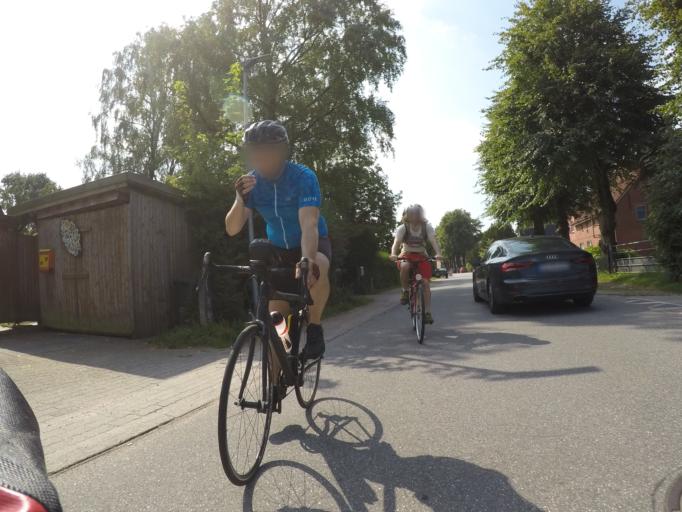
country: DE
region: Schleswig-Holstein
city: Tangstedt
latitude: 53.6999
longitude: 10.0491
